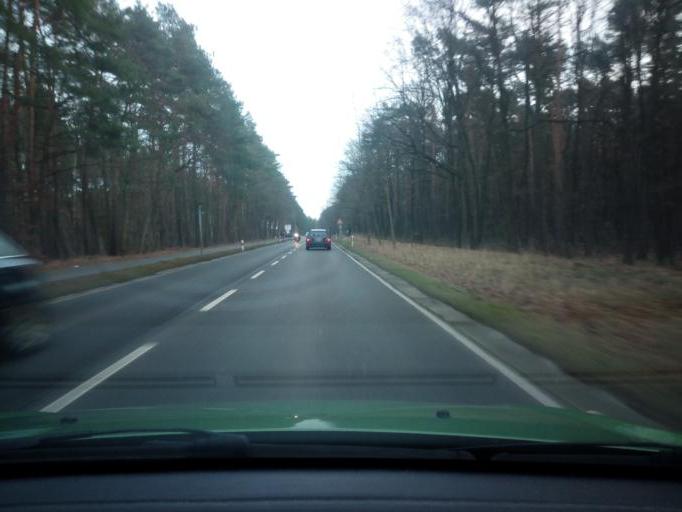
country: DE
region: Berlin
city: Muggelheim
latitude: 52.4222
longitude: 13.6380
